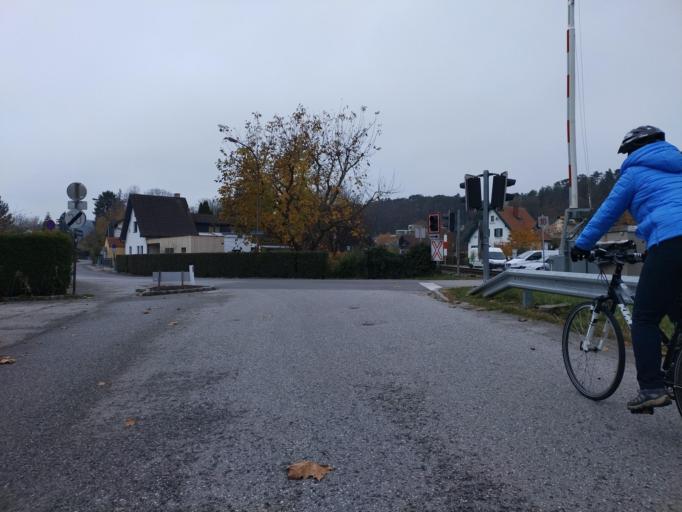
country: AT
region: Lower Austria
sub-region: Politischer Bezirk Neunkirchen
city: Pitten
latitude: 47.7223
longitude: 16.1873
